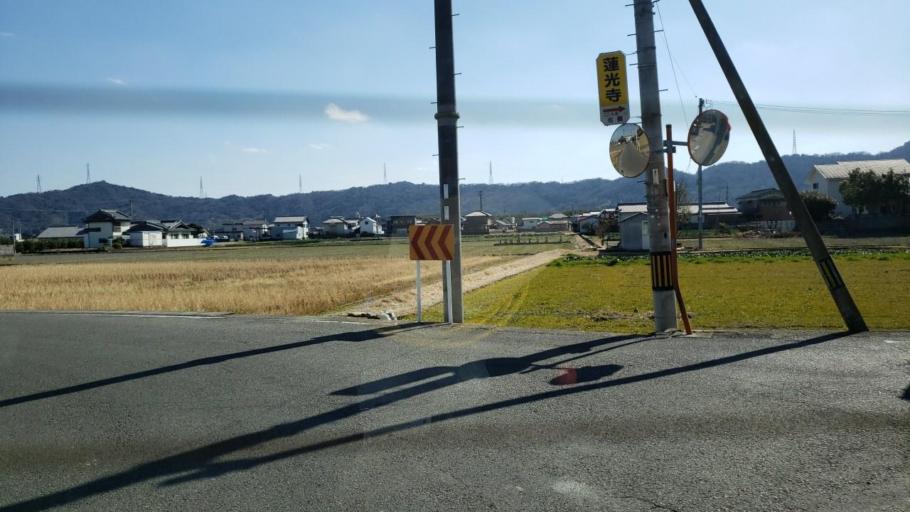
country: JP
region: Tokushima
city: Ishii
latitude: 34.0717
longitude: 134.4325
